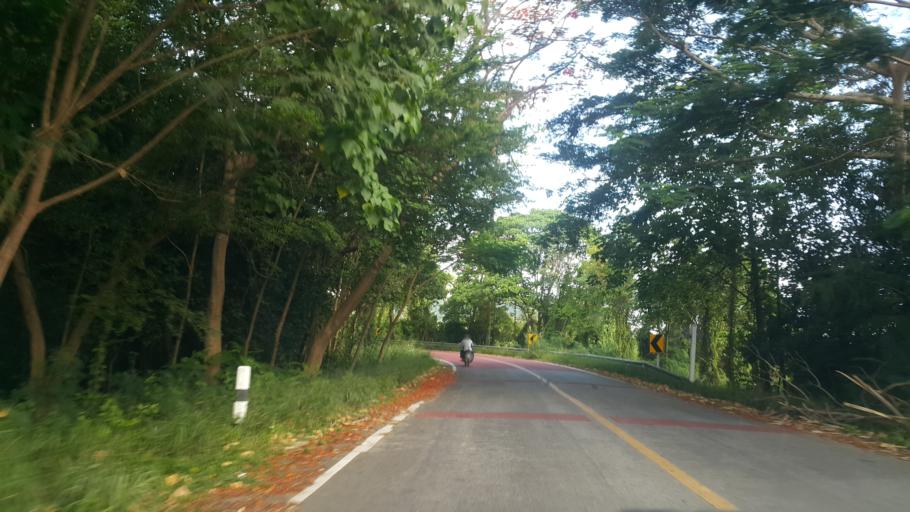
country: TH
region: Rayong
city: Ban Chang
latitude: 12.7868
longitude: 100.9566
